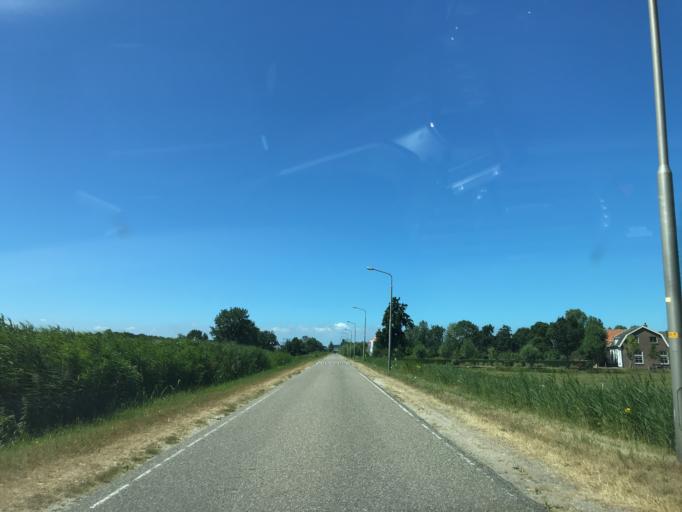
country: NL
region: North Holland
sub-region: Gemeente Naarden
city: Naarden
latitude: 52.3095
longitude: 5.1274
